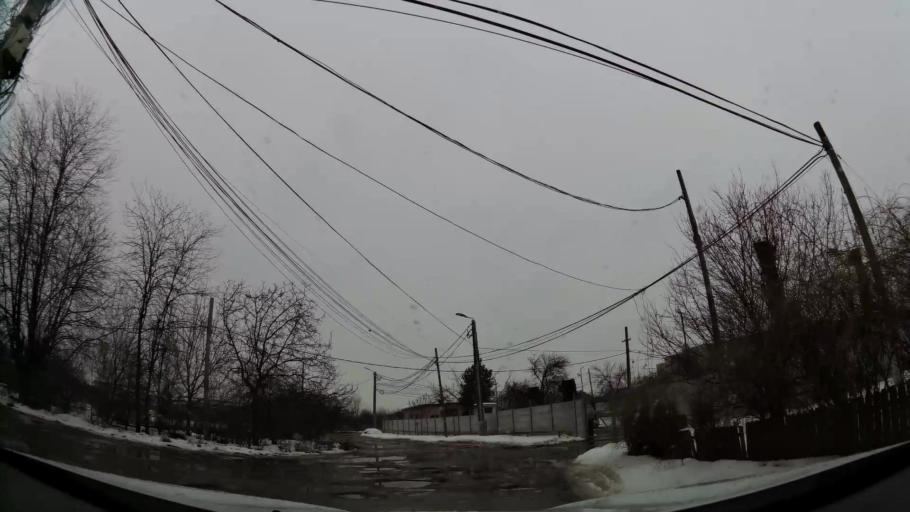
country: RO
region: Ilfov
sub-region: Comuna Chiajna
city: Rosu
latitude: 44.4063
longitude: 26.0117
